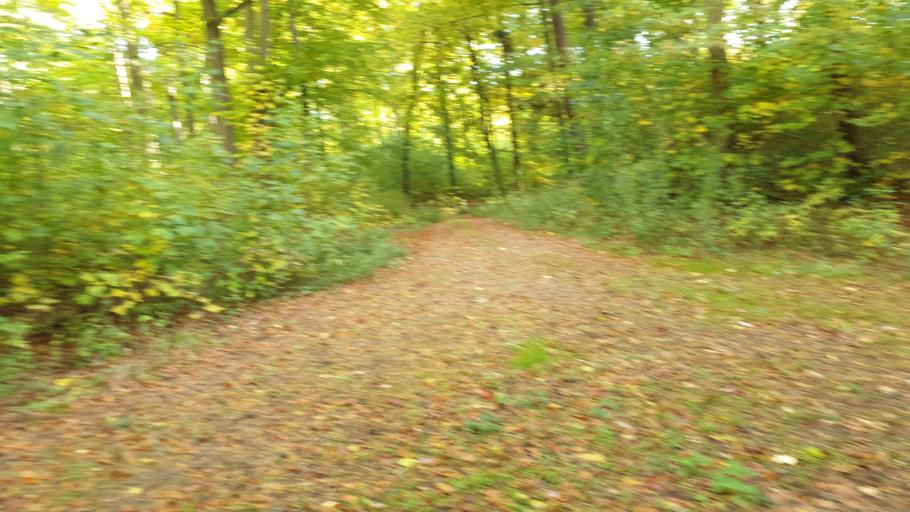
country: DE
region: Brandenburg
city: Liepe
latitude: 52.8720
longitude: 13.9531
